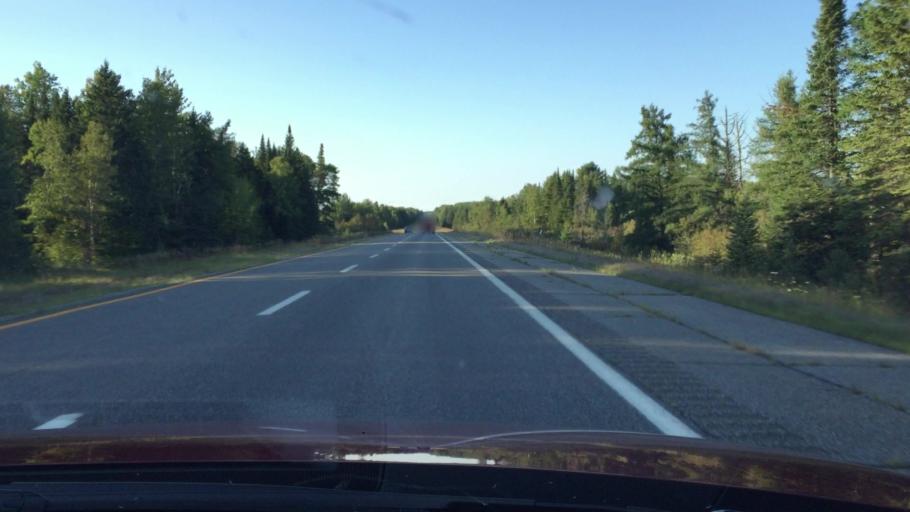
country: US
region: Maine
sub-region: Penobscot County
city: Patten
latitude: 45.8170
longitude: -68.4296
